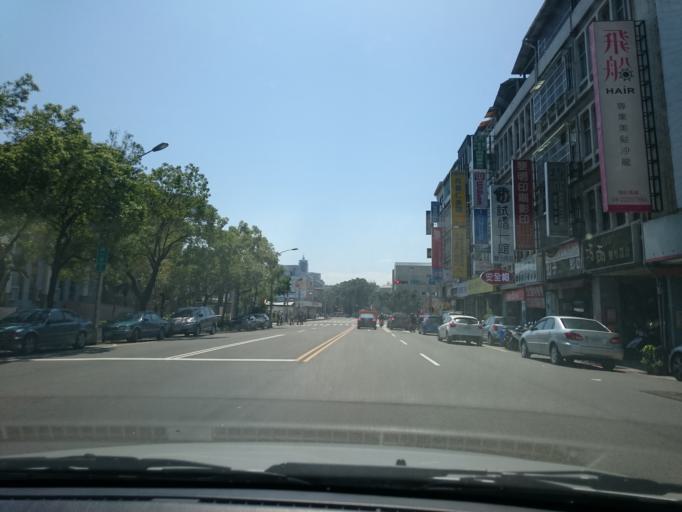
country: TW
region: Taiwan
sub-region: Taichung City
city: Taichung
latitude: 24.1480
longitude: 120.6867
